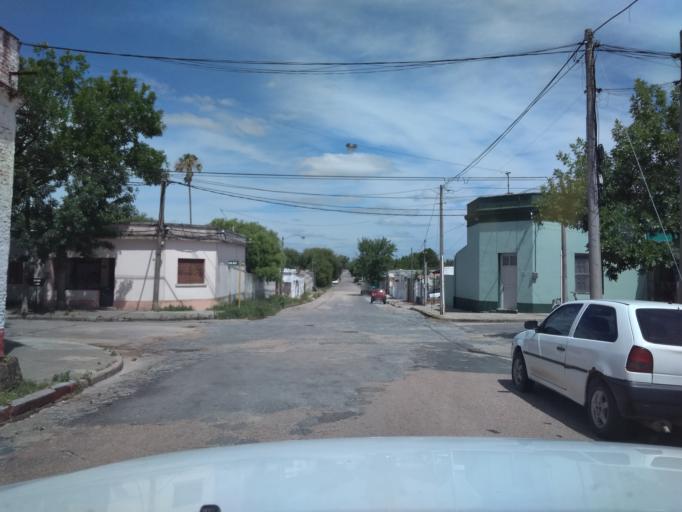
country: UY
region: Florida
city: Florida
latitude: -34.1048
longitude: -56.2171
